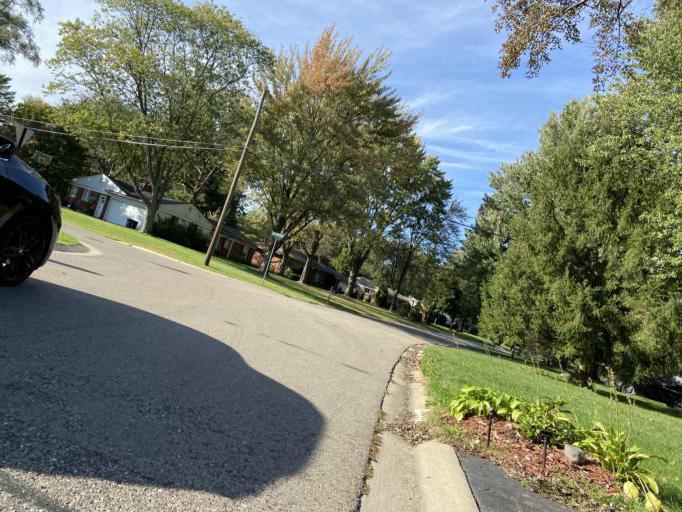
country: US
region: Michigan
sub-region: Oakland County
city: Farmington Hills
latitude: 42.5028
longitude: -83.3756
